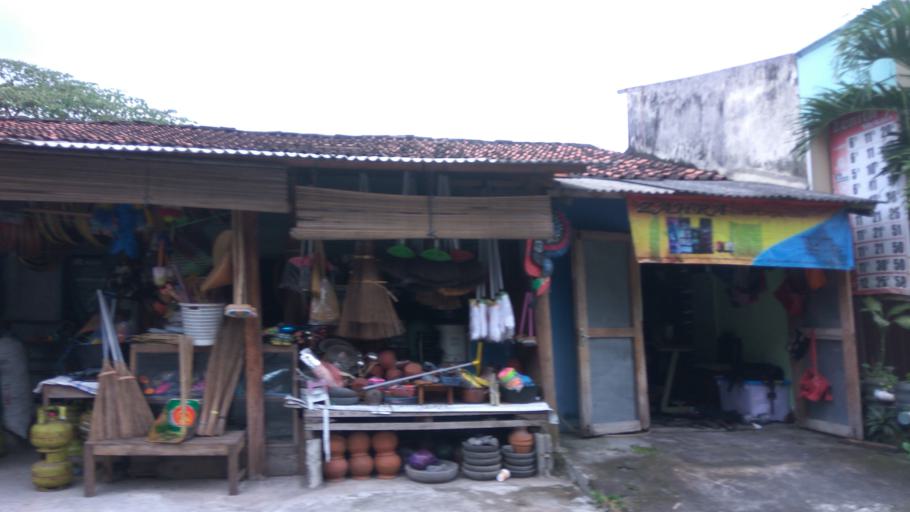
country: ID
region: Daerah Istimewa Yogyakarta
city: Depok
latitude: -7.7363
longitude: 110.4074
